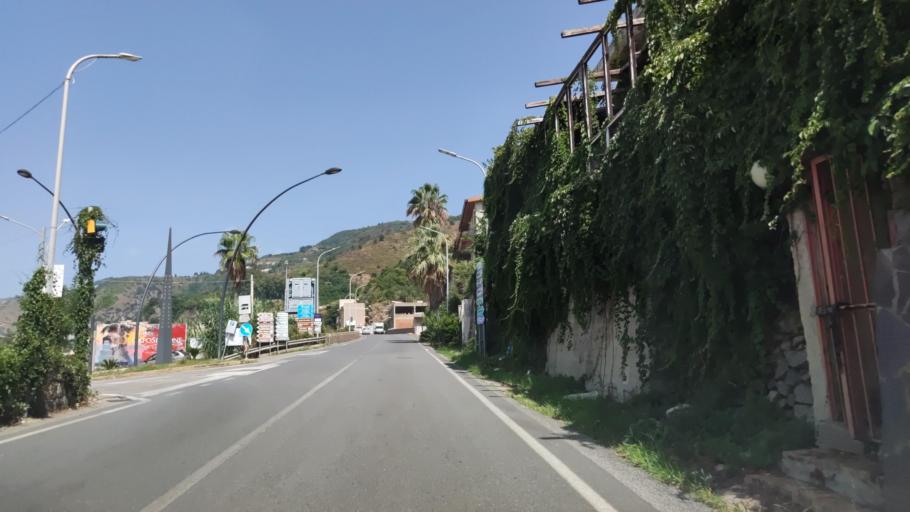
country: IT
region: Calabria
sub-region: Provincia di Reggio Calabria
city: Bagnara Calabra
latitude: 38.2803
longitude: 15.7980
